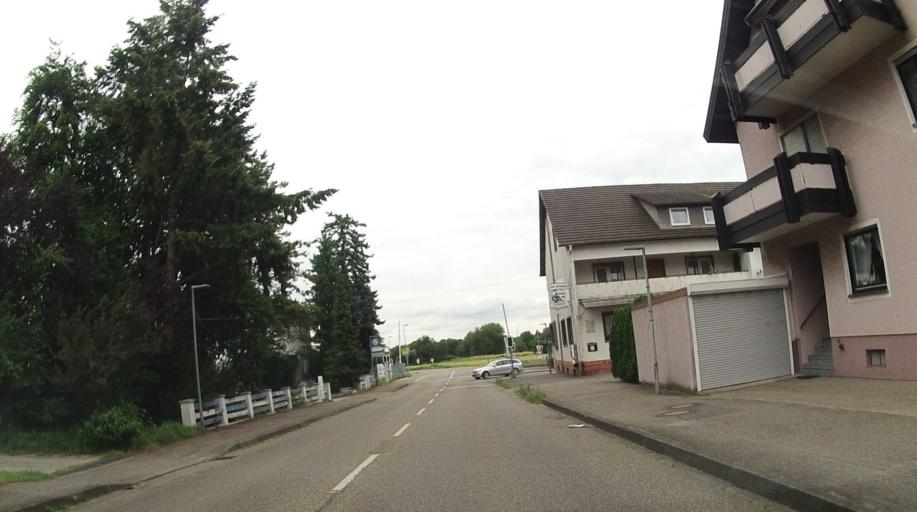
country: DE
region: Baden-Wuerttemberg
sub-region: Karlsruhe Region
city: Kuppenheim
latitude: 48.8340
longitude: 8.2547
